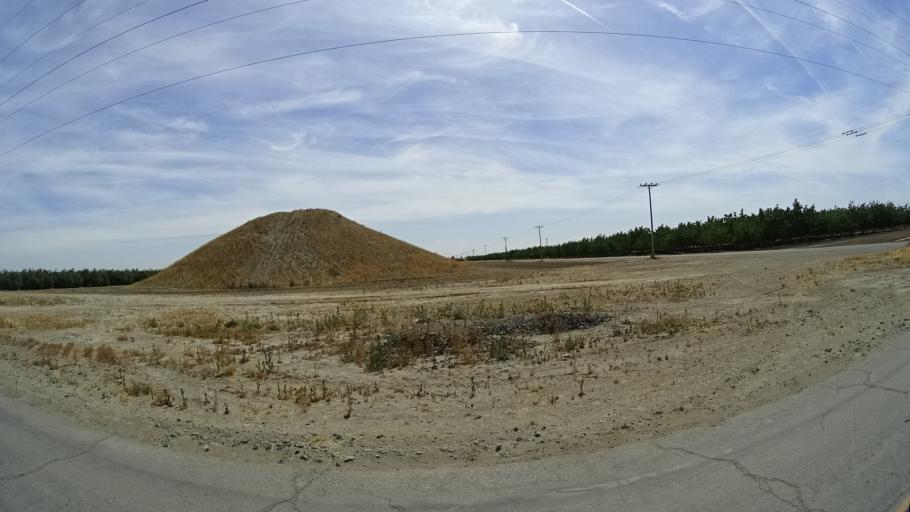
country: US
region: California
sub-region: Kings County
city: Hanford
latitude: 36.3575
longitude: -119.5921
